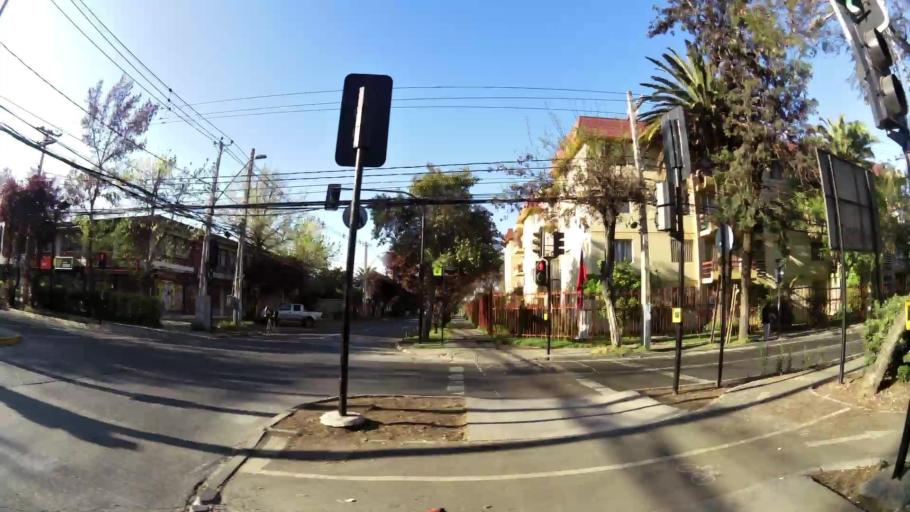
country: CL
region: Santiago Metropolitan
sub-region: Provincia de Santiago
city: Villa Presidente Frei, Nunoa, Santiago, Chile
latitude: -33.4532
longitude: -70.5672
